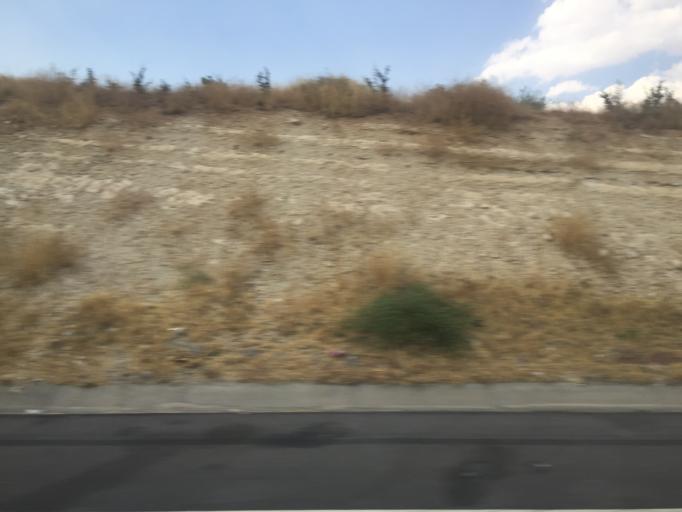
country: TR
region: Sanliurfa
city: Akziyaret
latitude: 37.2689
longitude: 38.7902
